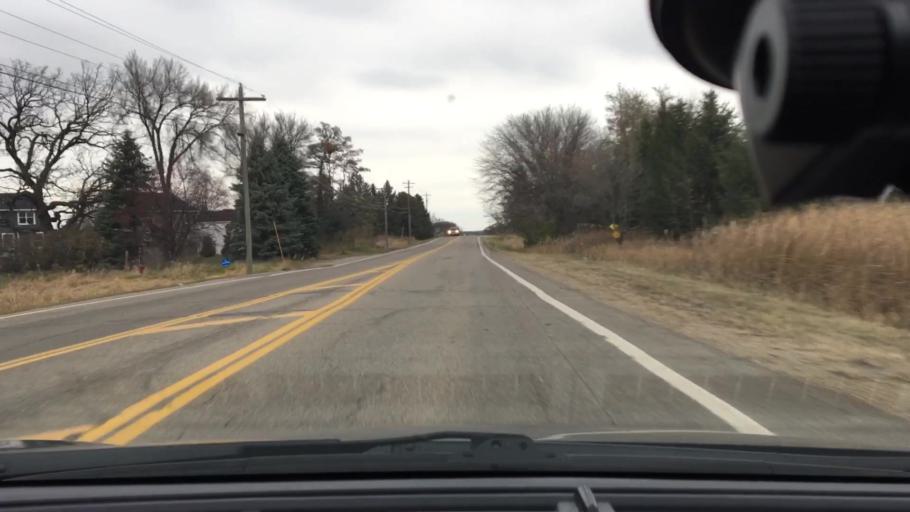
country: US
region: Minnesota
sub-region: Hennepin County
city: Corcoran
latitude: 45.0740
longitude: -93.5220
